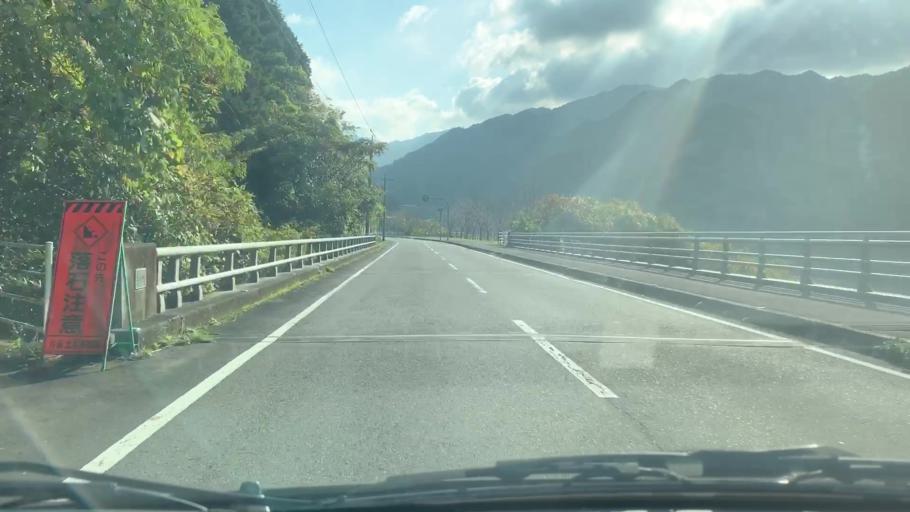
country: JP
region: Saga Prefecture
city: Kashima
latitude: 33.0375
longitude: 130.0708
